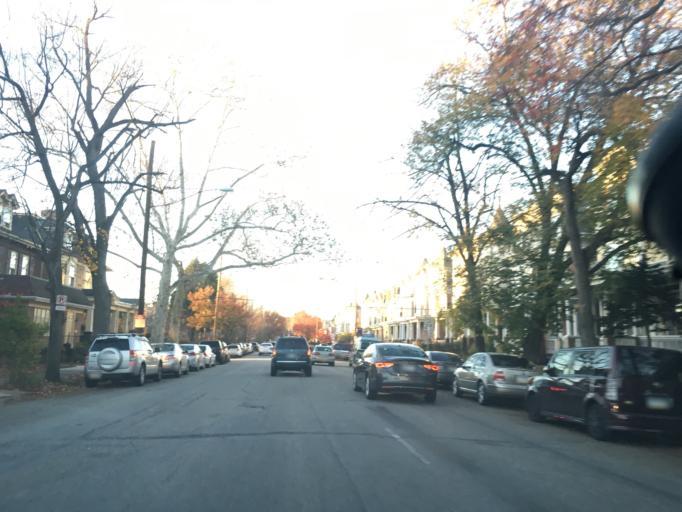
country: US
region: Pennsylvania
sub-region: Dauphin County
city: Harrisburg
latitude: 40.2755
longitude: -76.8966
